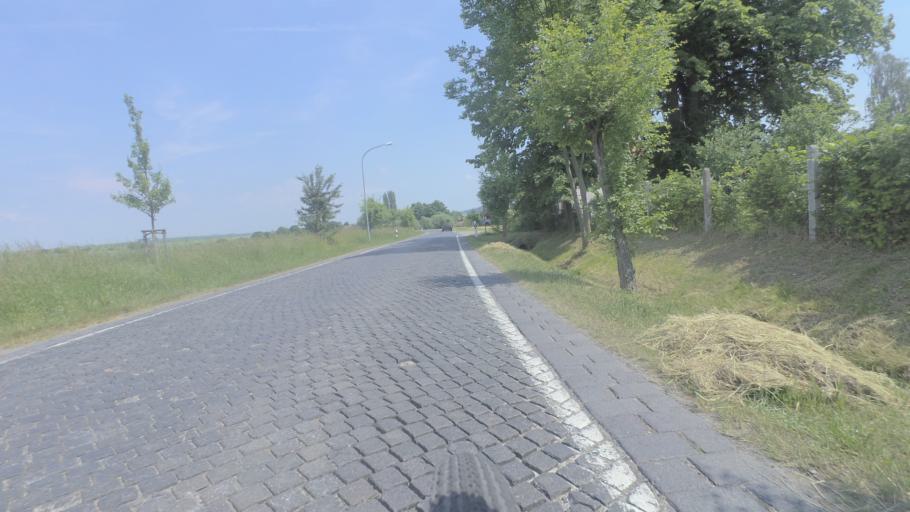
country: DE
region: Saxony-Anhalt
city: Ballenstedt
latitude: 51.7180
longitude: 11.2582
